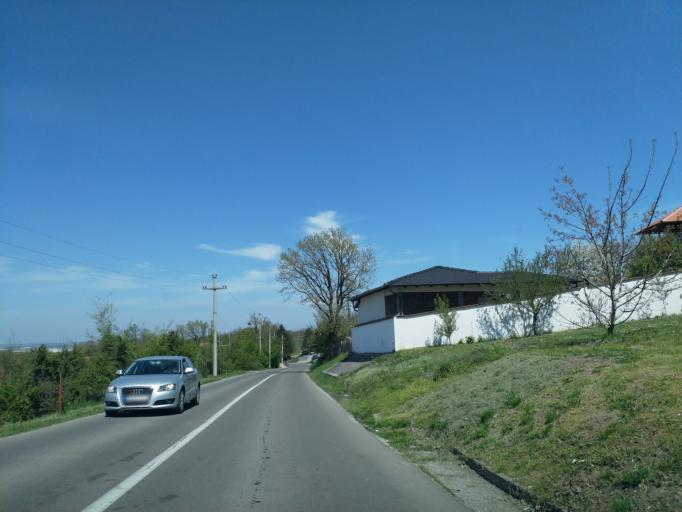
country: RS
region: Central Serbia
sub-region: Belgrade
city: Lazarevac
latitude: 44.3701
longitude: 20.3015
